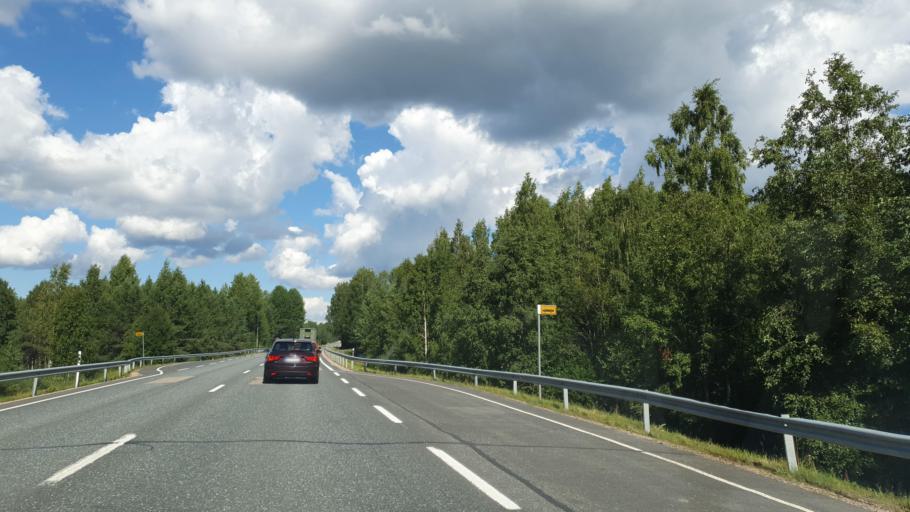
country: FI
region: Kainuu
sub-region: Kajaani
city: Kajaani
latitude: 64.1072
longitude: 27.4481
